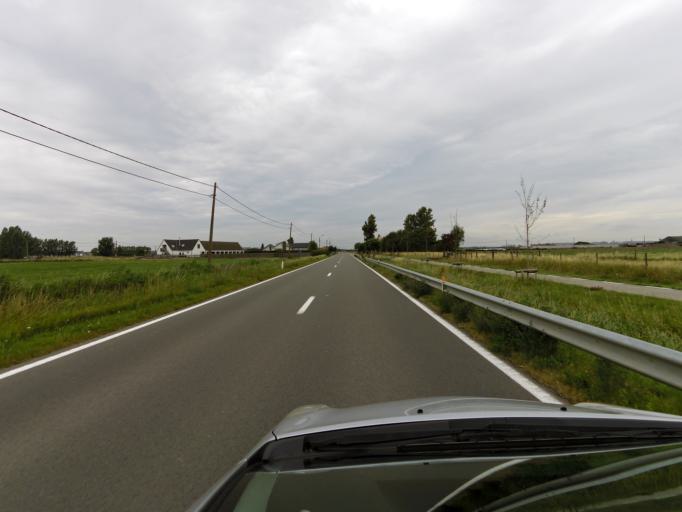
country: BE
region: Flanders
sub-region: Provincie West-Vlaanderen
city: Wenduine
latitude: 51.2855
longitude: 3.0891
